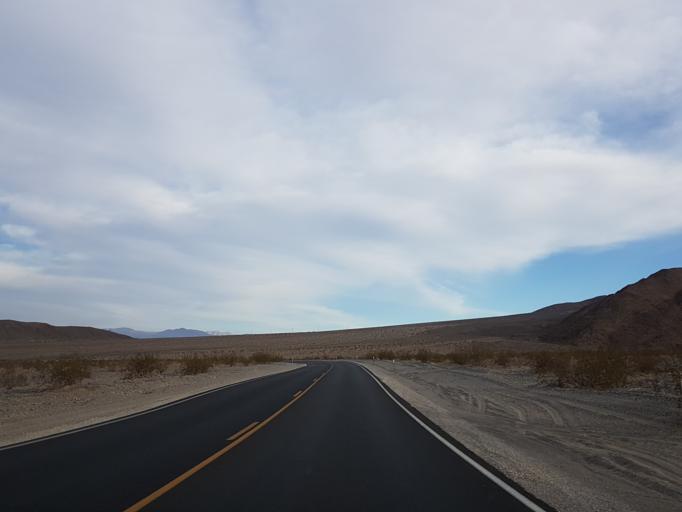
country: US
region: Nevada
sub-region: Nye County
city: Beatty
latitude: 36.6022
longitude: -117.1003
